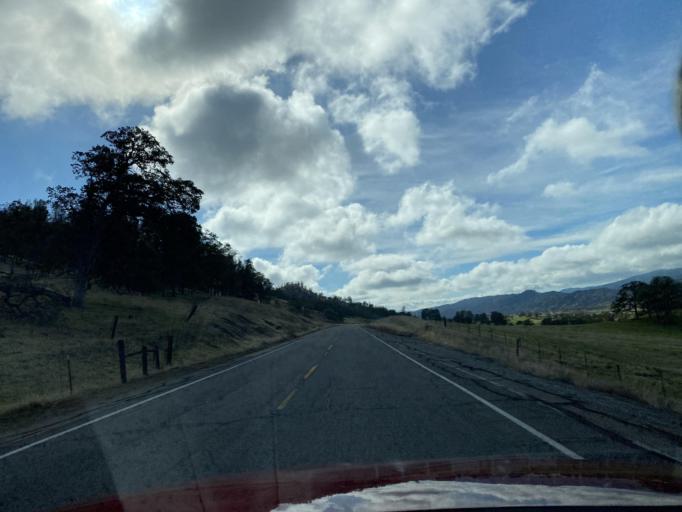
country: US
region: California
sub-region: Glenn County
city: Willows
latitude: 39.5700
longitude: -122.5400
